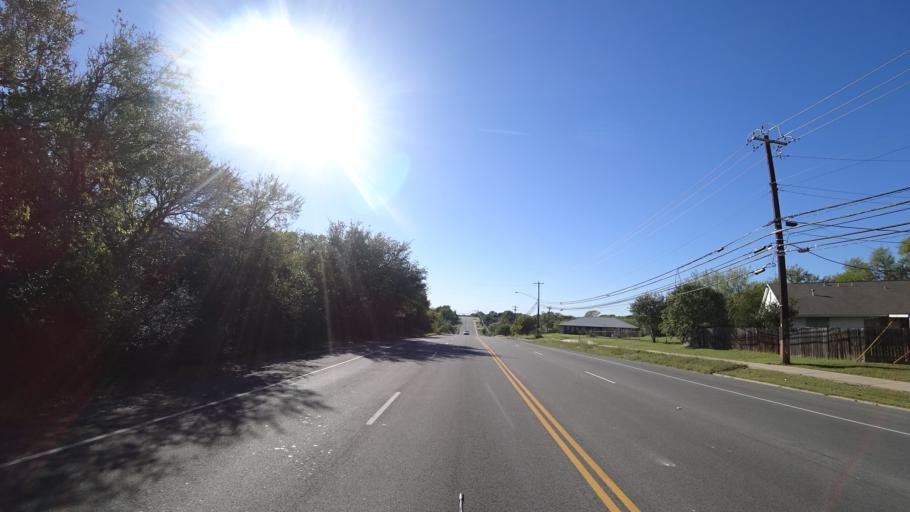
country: US
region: Texas
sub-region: Travis County
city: Austin
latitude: 30.2865
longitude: -97.6754
